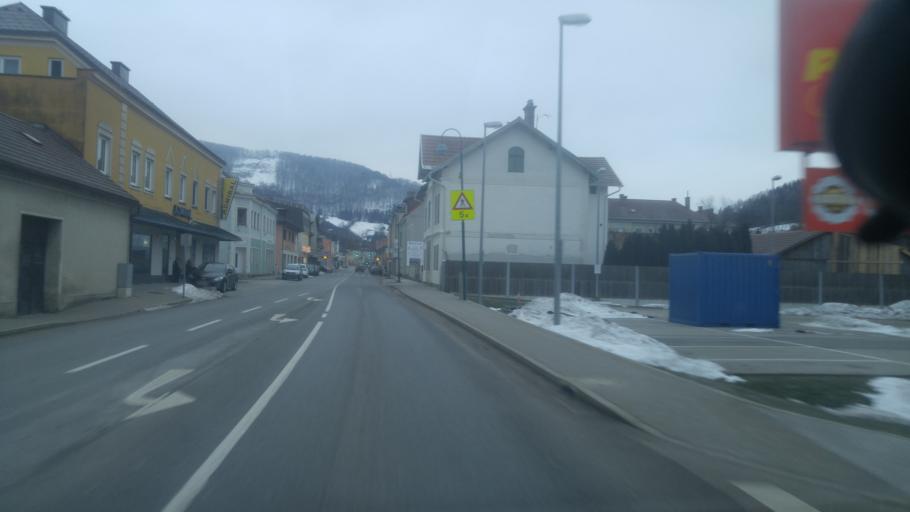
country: AT
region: Lower Austria
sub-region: Politischer Bezirk Lilienfeld
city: Traisen
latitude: 48.0441
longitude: 15.6090
